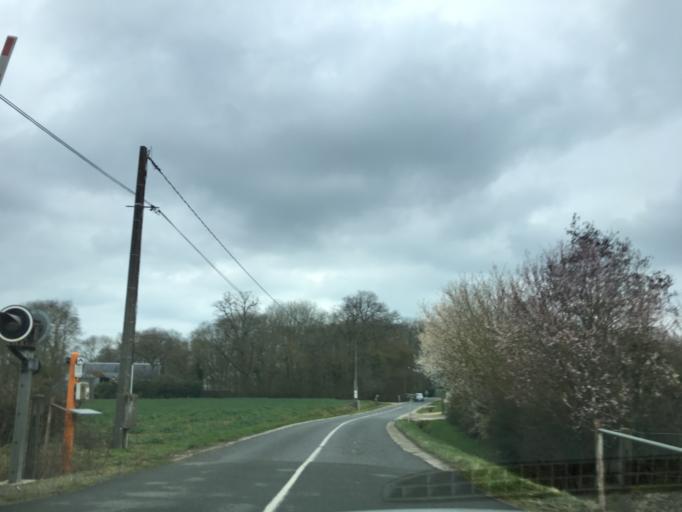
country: FR
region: Centre
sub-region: Departement d'Indre-et-Loire
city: Chanceaux-sur-Choisille
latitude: 47.4706
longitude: 0.7334
